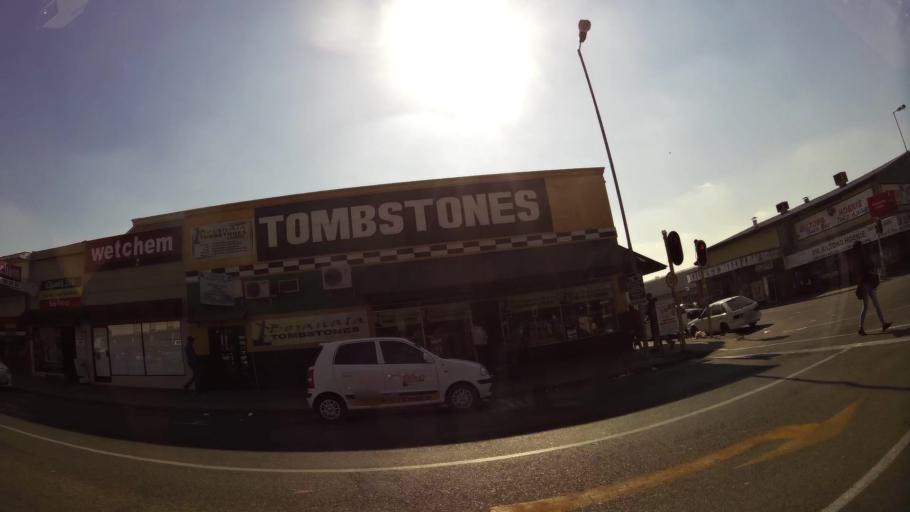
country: ZA
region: North-West
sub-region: Bojanala Platinum District Municipality
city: Rustenburg
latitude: -25.6716
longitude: 27.2446
